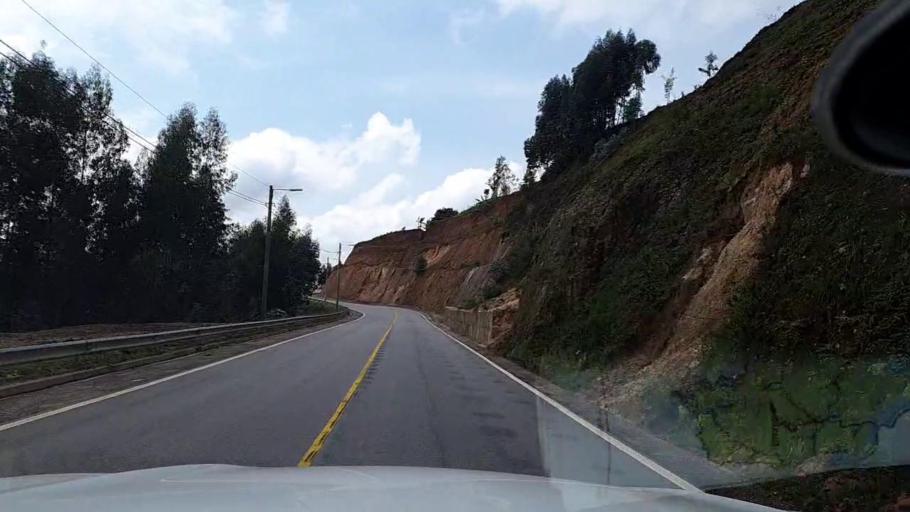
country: RW
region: Southern Province
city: Nzega
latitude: -2.5186
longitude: 29.4588
